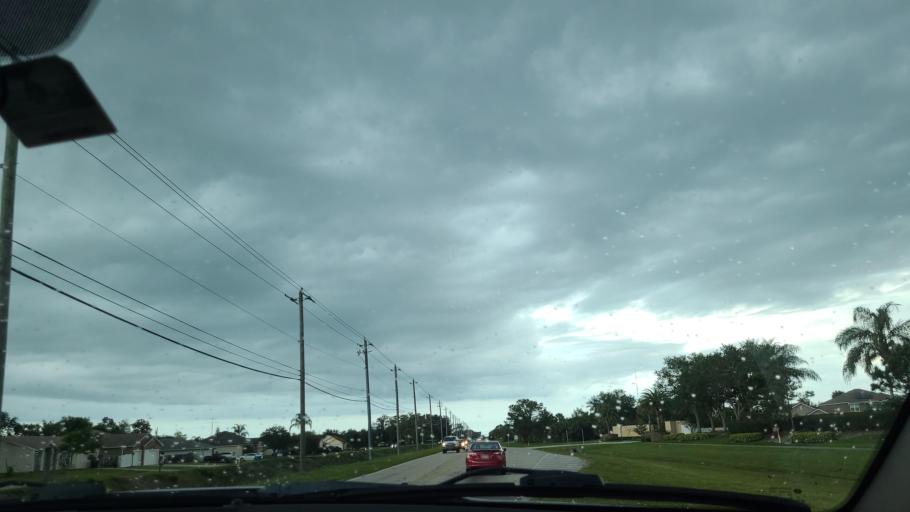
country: US
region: Florida
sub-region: Brevard County
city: June Park
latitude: 27.9991
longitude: -80.6842
